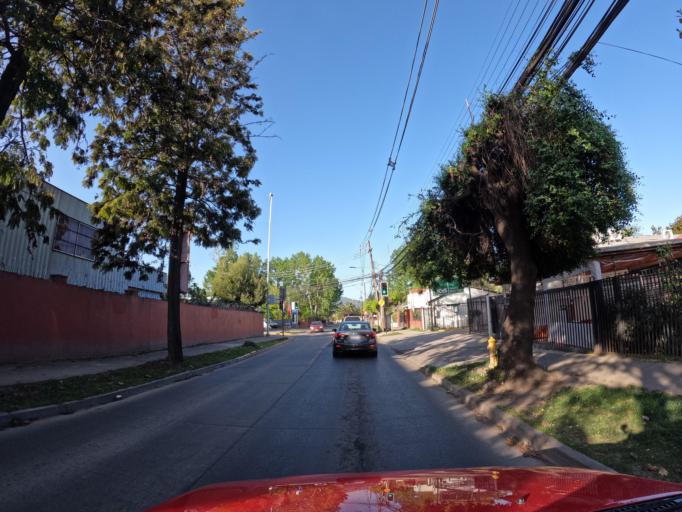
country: CL
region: O'Higgins
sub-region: Provincia de Colchagua
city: Santa Cruz
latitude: -34.6427
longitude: -71.3654
